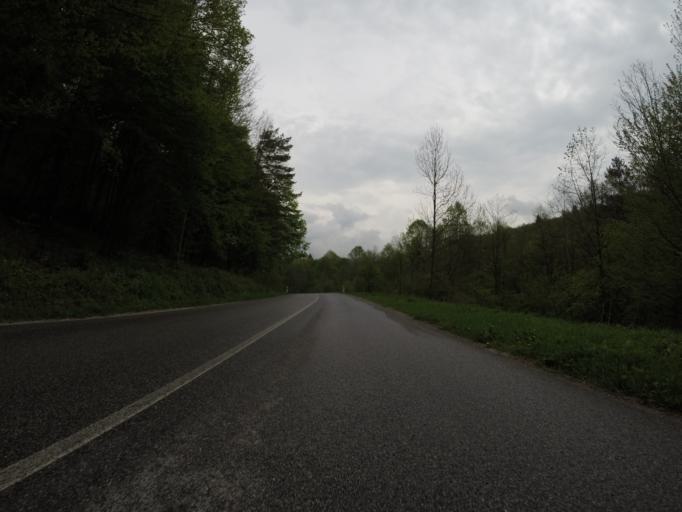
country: SK
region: Banskobystricky
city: Tisovec
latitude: 48.7215
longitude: 20.0093
